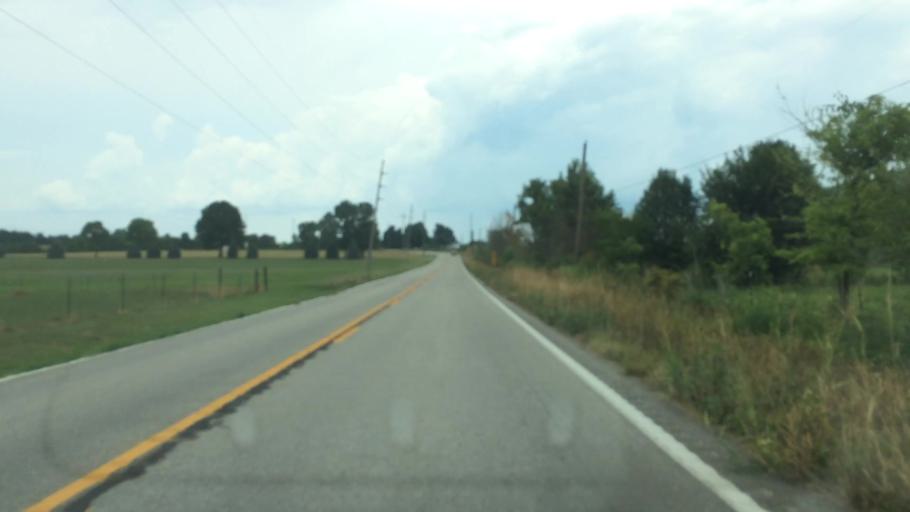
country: US
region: Missouri
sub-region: Greene County
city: Strafford
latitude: 37.2489
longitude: -93.1354
